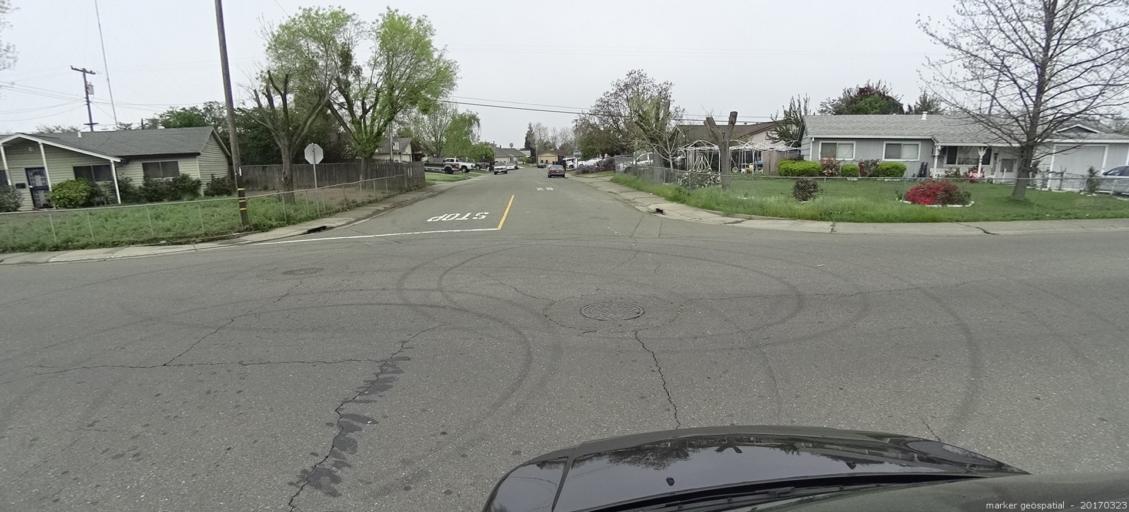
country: US
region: California
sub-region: Sacramento County
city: Florin
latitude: 38.5038
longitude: -121.4166
